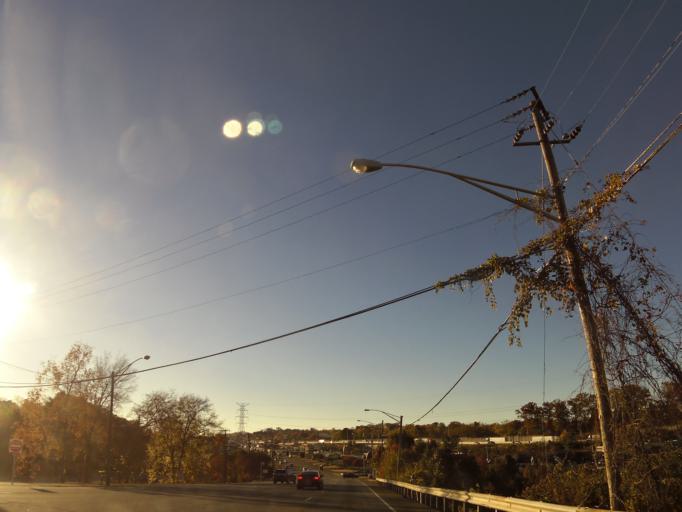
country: US
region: Tennessee
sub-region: Knox County
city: Knoxville
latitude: 35.9326
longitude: -84.0163
